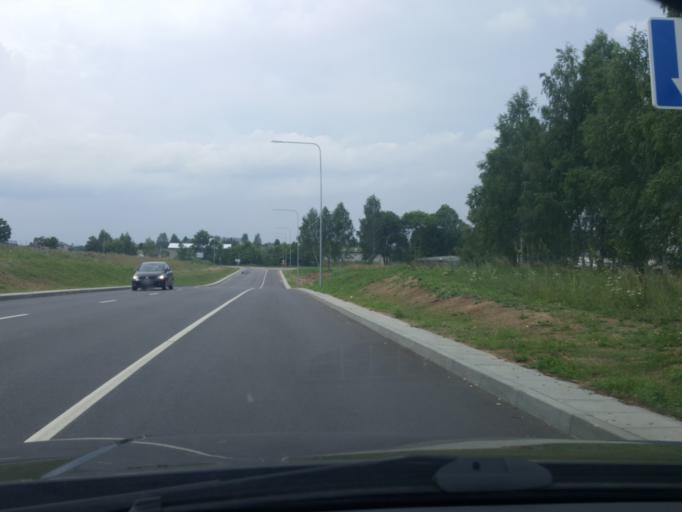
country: LT
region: Alytaus apskritis
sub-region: Alytus
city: Alytus
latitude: 54.4380
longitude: 24.0099
